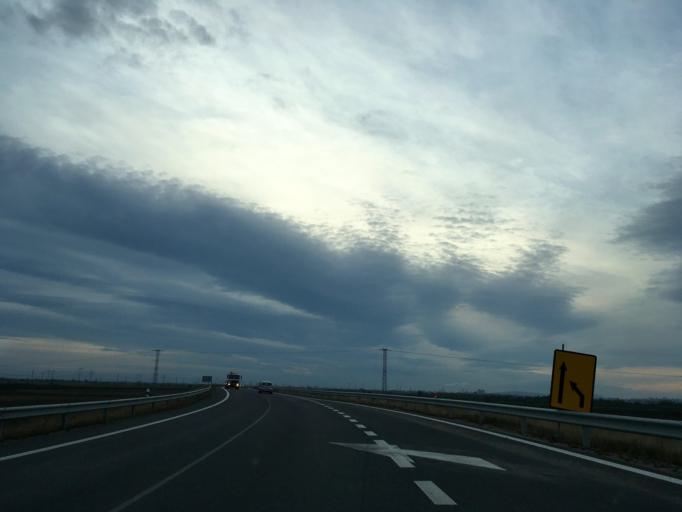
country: SK
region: Bratislavsky
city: Dunajska Luzna
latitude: 48.1303
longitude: 17.2855
